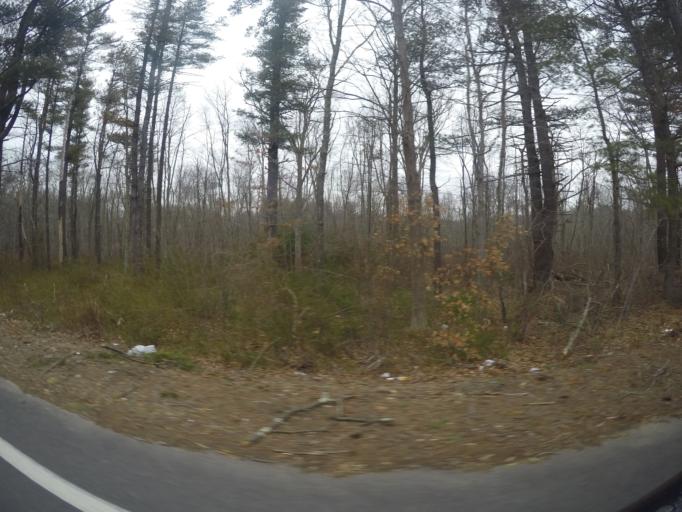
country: US
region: Massachusetts
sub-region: Bristol County
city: Easton
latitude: 42.0137
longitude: -71.0892
